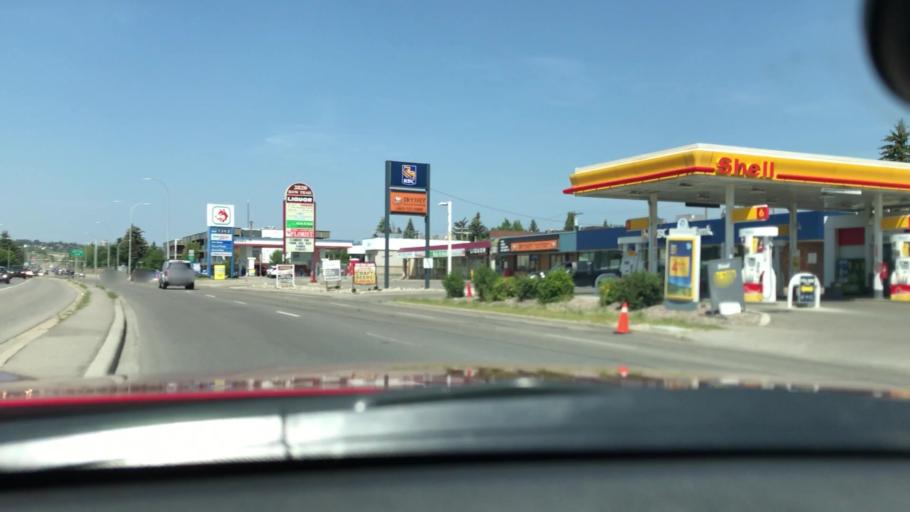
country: CA
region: Alberta
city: Calgary
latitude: 51.0453
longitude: -114.1415
